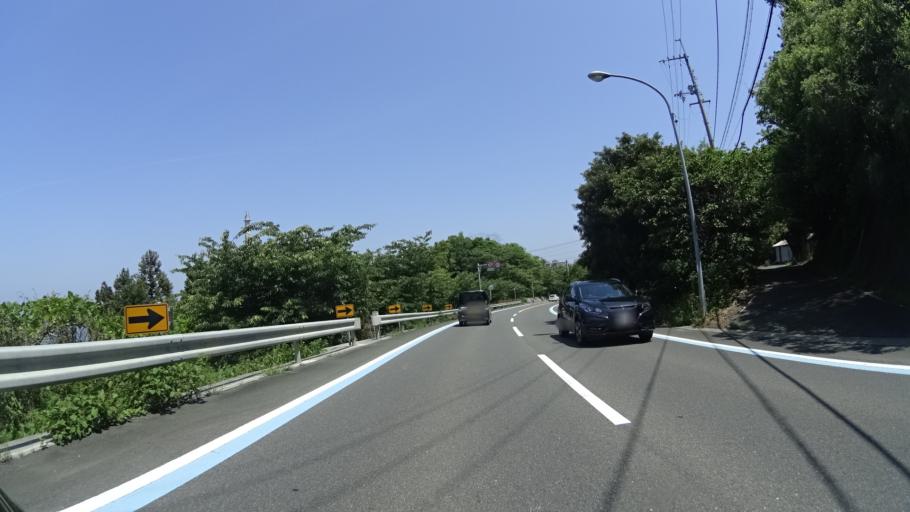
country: JP
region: Ehime
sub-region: Nishiuwa-gun
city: Ikata-cho
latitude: 33.5343
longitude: 132.3992
